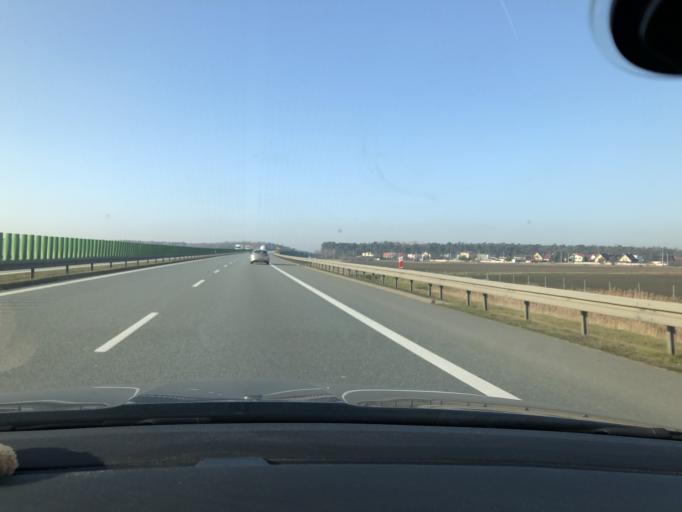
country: PL
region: Greater Poland Voivodeship
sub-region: Powiat poznanski
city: Dopiewo
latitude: 52.3484
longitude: 16.6752
